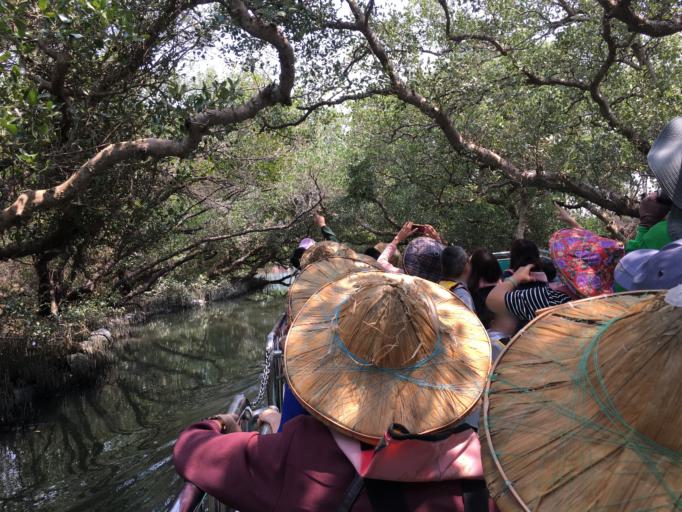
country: TW
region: Taiwan
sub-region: Tainan
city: Tainan
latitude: 23.0250
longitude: 120.1351
